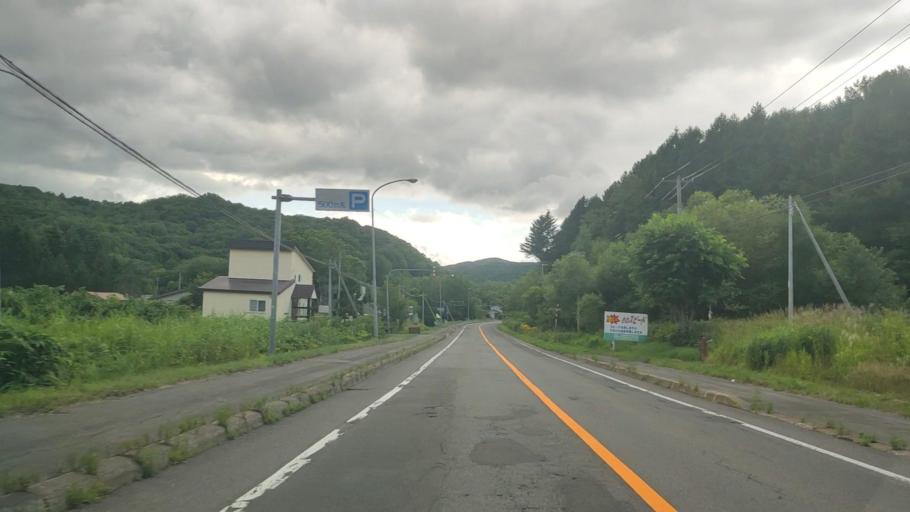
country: JP
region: Hokkaido
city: Date
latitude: 42.6375
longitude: 141.0393
